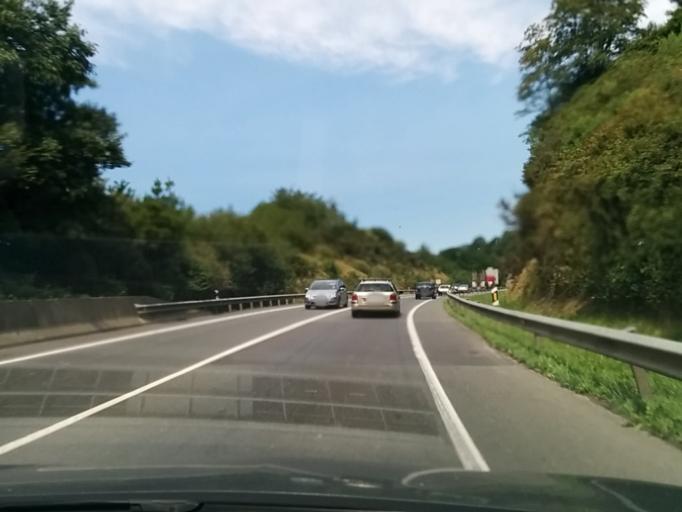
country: ES
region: Basque Country
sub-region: Provincia de Guipuzcoa
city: Errenteria
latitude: 43.3117
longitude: -1.8908
